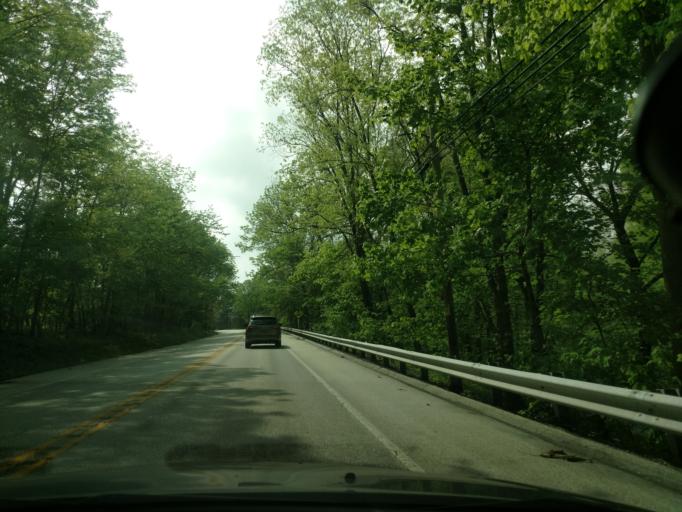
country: US
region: Pennsylvania
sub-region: Montgomery County
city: Stowe
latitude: 40.1754
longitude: -75.7099
